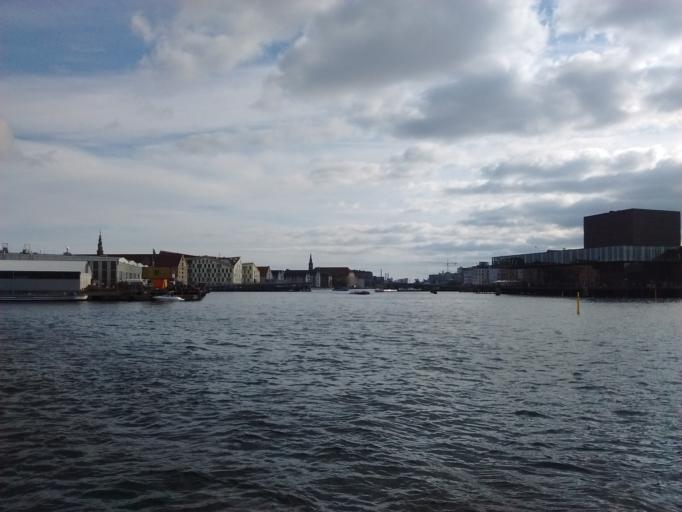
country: DK
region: Capital Region
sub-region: Kobenhavn
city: Christianshavn
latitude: 55.6811
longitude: 12.5988
